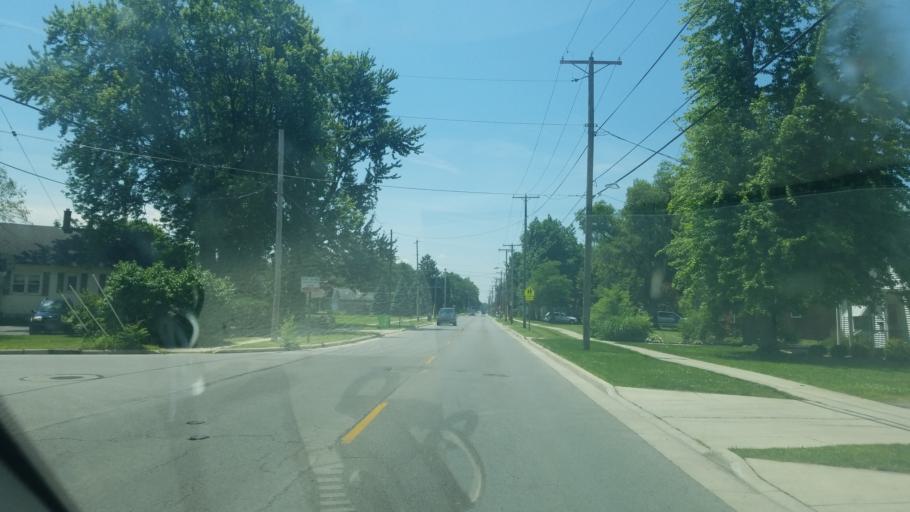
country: US
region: Ohio
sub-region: Hancock County
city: Findlay
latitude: 41.0591
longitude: -83.6371
